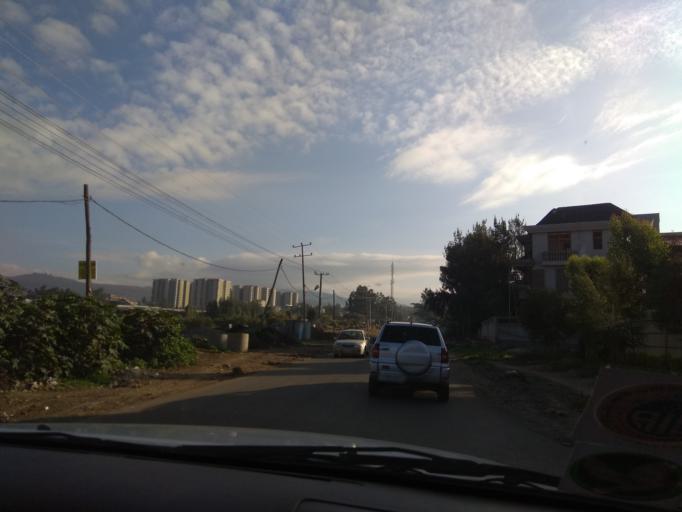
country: ET
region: Adis Abeba
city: Addis Ababa
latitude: 8.9944
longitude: 38.8039
